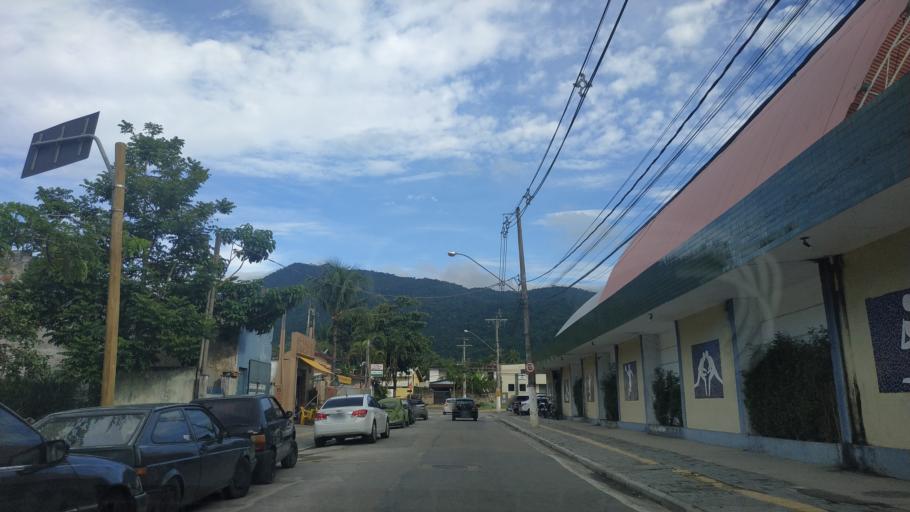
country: BR
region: Sao Paulo
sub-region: Ilhabela
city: Ilhabela
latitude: -23.8228
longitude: -45.3673
